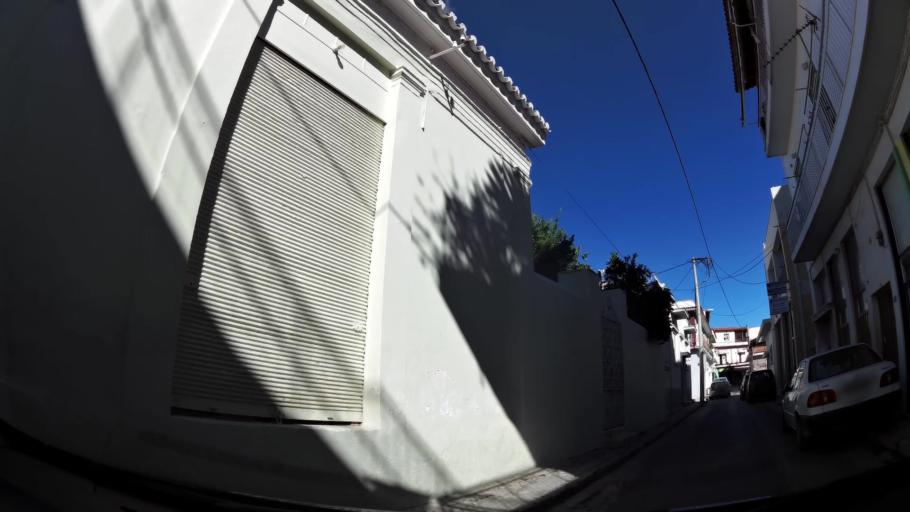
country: GR
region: Attica
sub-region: Nomarchia Anatolikis Attikis
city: Koropi
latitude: 37.8994
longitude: 23.8721
